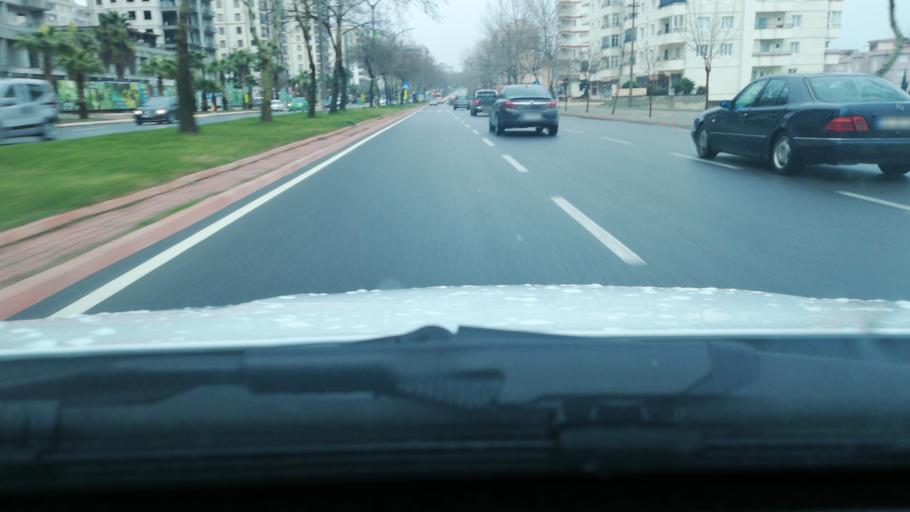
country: TR
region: Kahramanmaras
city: Kahramanmaras
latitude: 37.5923
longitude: 36.8647
